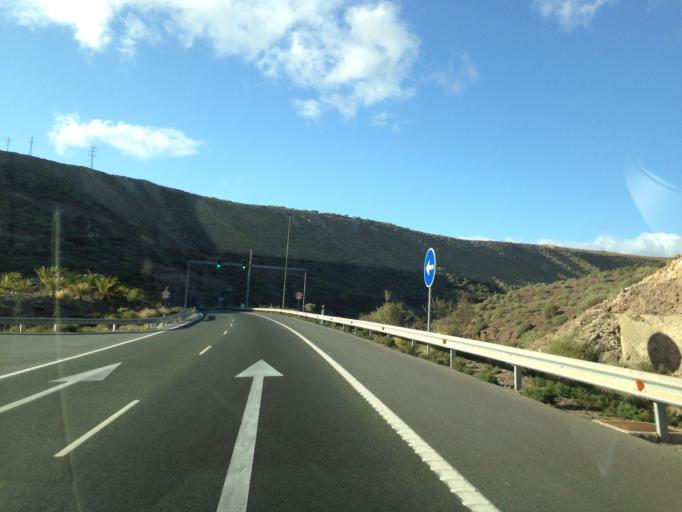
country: ES
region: Canary Islands
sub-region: Provincia de Las Palmas
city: Puerto Rico
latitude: 27.7828
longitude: -15.6788
